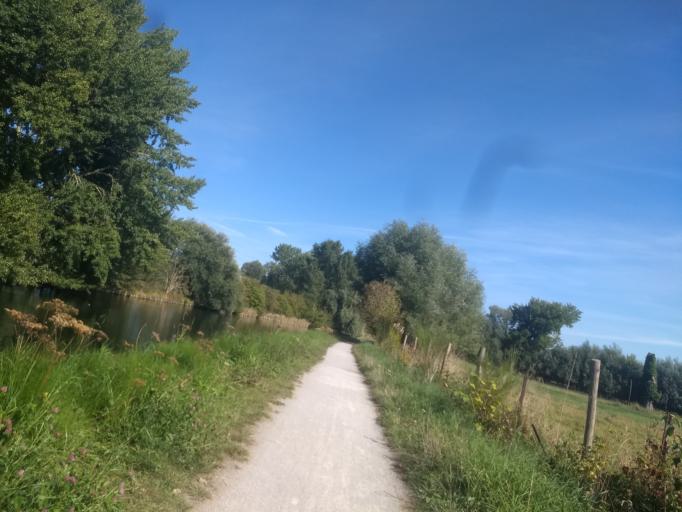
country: FR
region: Nord-Pas-de-Calais
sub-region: Departement du Pas-de-Calais
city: Feuchy
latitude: 50.2979
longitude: 2.8416
